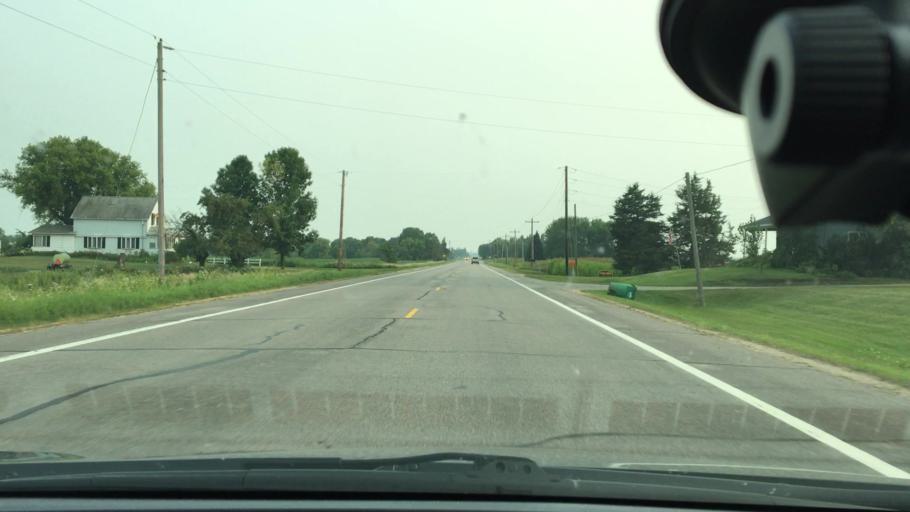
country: US
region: Minnesota
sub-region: Wright County
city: Albertville
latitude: 45.2713
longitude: -93.6636
